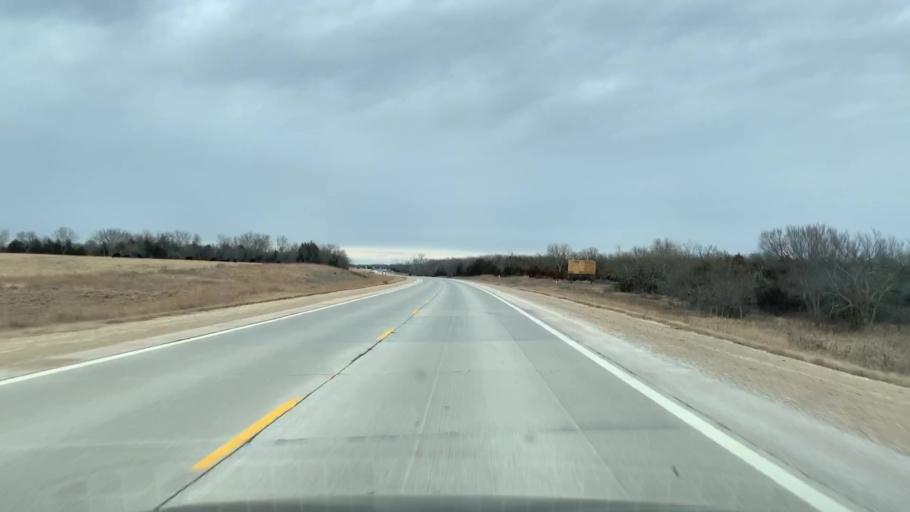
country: US
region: Kansas
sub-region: Allen County
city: Iola
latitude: 37.8974
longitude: -95.3834
